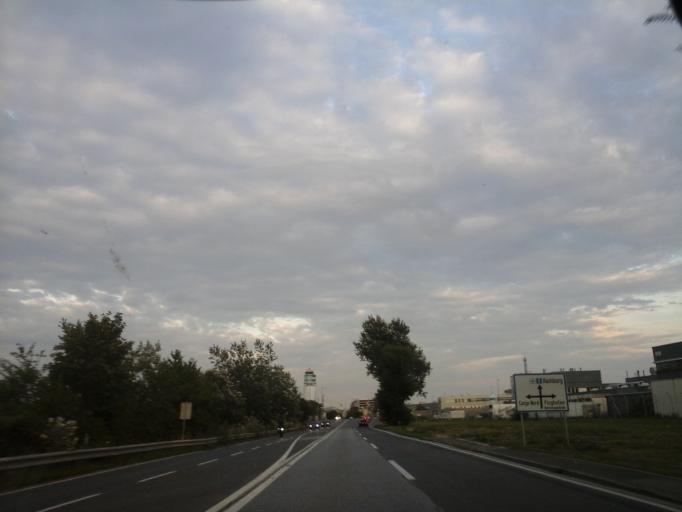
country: AT
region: Lower Austria
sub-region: Politischer Bezirk Wien-Umgebung
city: Rauchenwarth
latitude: 48.1282
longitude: 16.5459
